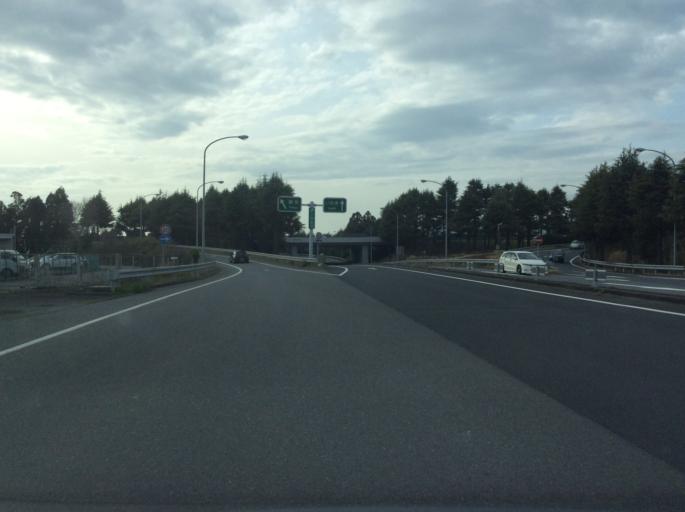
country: JP
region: Ibaraki
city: Naka
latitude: 36.1189
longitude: 140.1868
